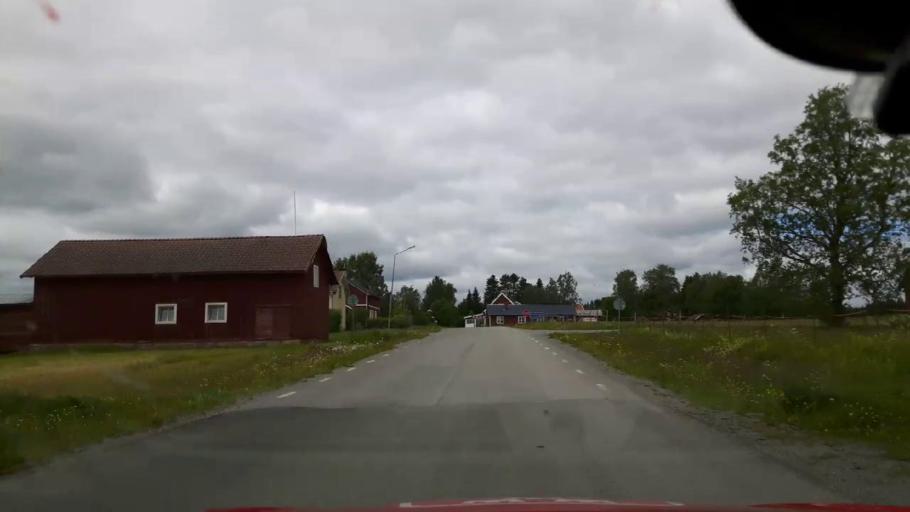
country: SE
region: Jaemtland
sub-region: OEstersunds Kommun
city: Brunflo
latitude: 63.0801
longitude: 14.8721
